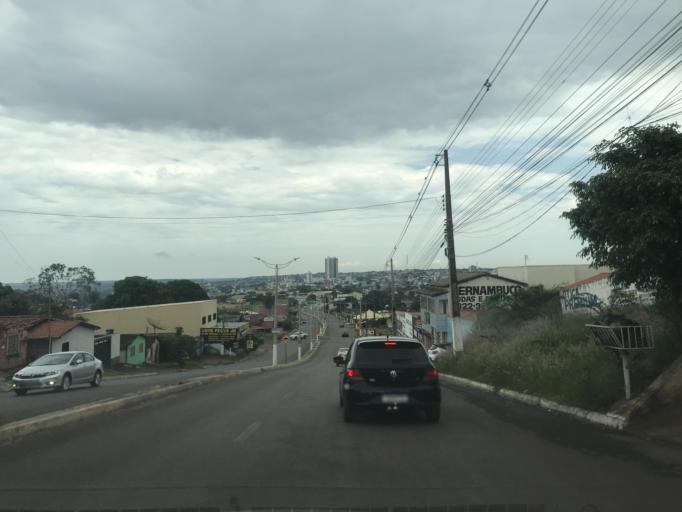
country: BR
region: Goias
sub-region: Luziania
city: Luziania
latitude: -16.2404
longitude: -47.9436
